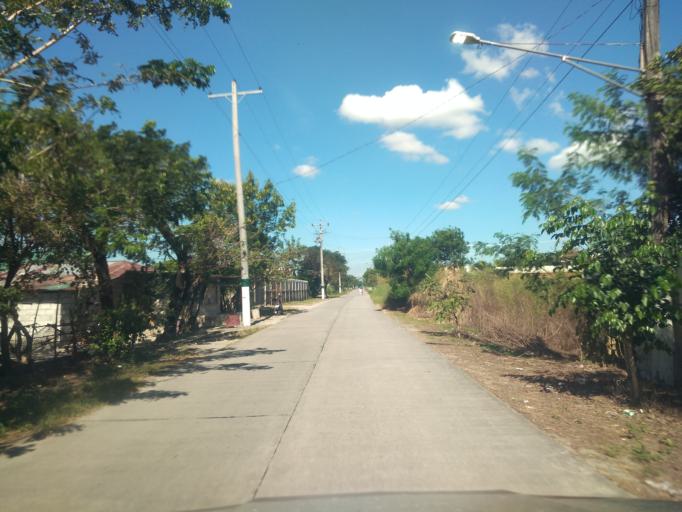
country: PH
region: Central Luzon
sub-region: Province of Pampanga
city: Bacolor
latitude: 15.0110
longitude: 120.6362
